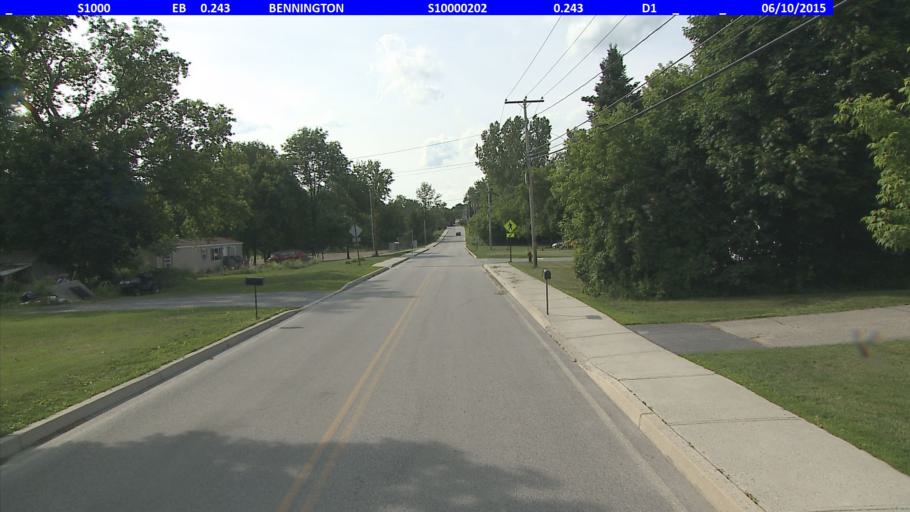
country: US
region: Vermont
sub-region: Bennington County
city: Bennington
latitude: 42.8721
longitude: -73.1783
